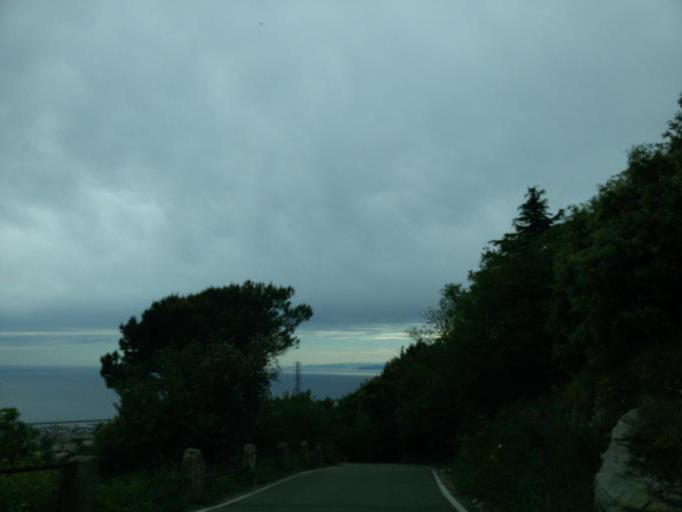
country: IT
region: Liguria
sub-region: Provincia di Genova
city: Genoa
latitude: 44.4366
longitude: 8.9190
